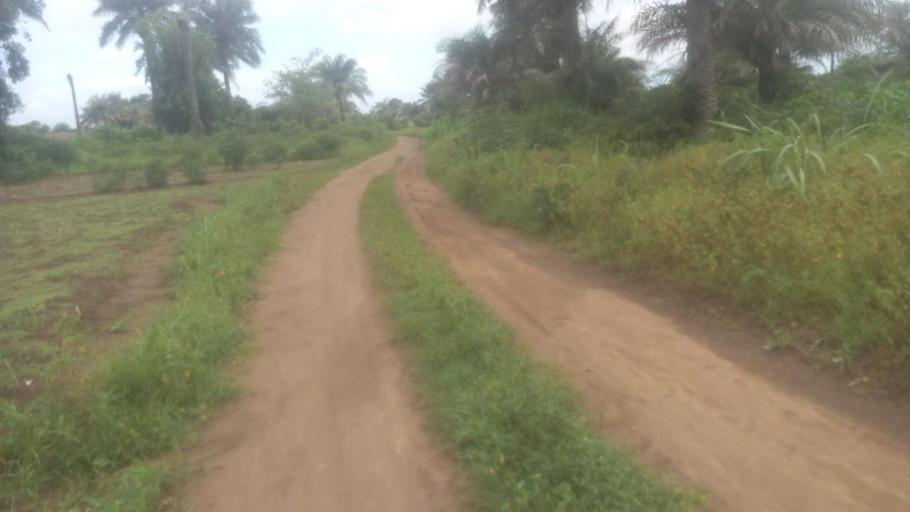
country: SL
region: Northern Province
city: Masoyila
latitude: 8.5933
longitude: -13.1926
